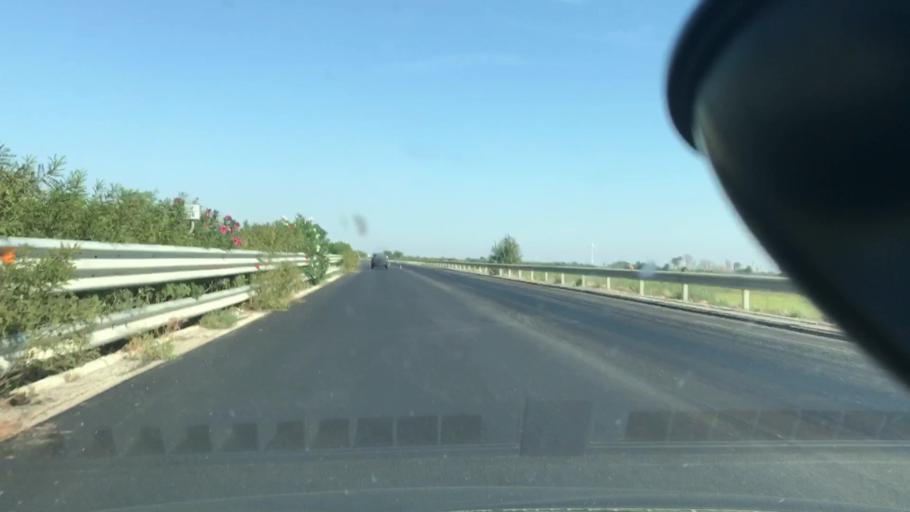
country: IT
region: Apulia
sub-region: Provincia di Foggia
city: Ascoli Satriano
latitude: 41.2767
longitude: 15.5536
